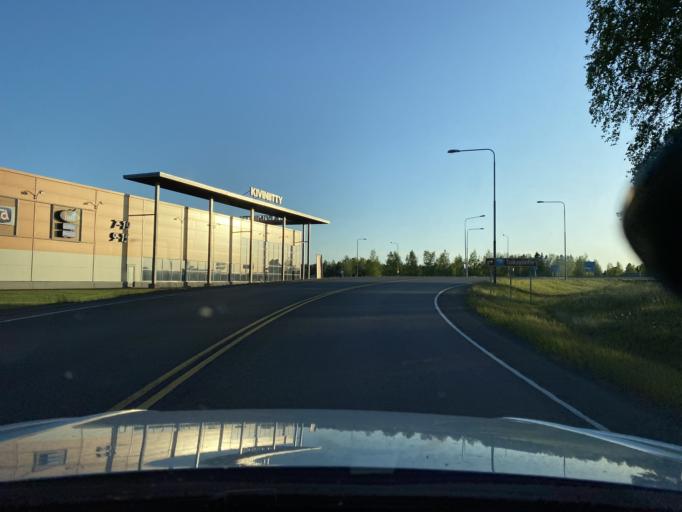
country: FI
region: Satakunta
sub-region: Pori
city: Huittinen
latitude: 61.1683
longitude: 22.6771
